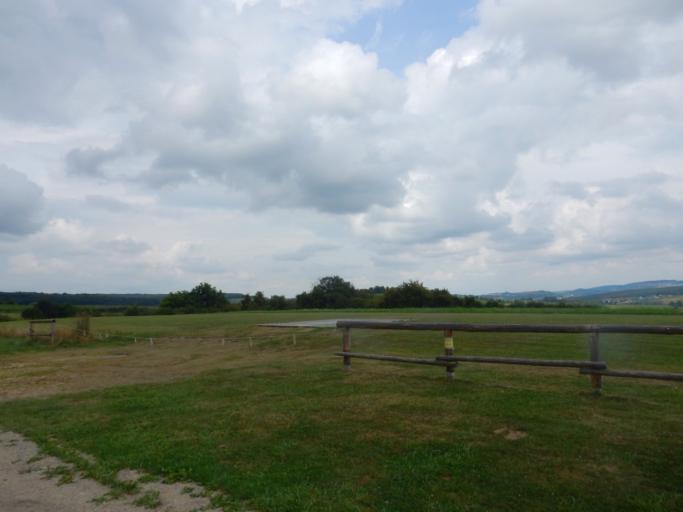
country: LU
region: Grevenmacher
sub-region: Canton de Remich
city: Stadtbredimus
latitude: 49.5698
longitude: 6.3520
